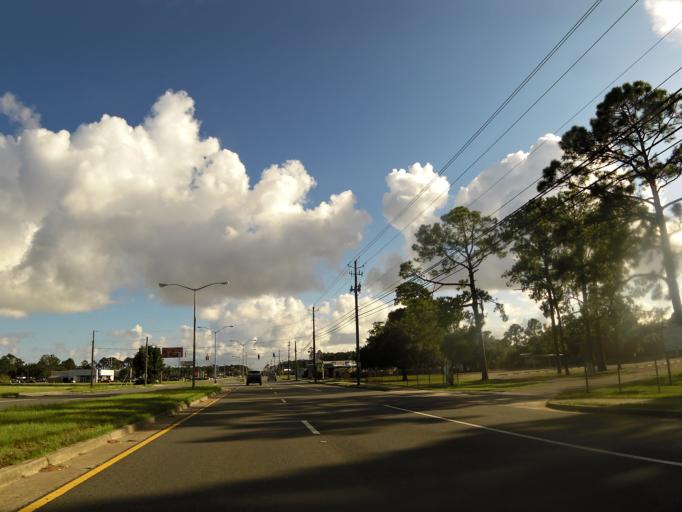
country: US
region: Georgia
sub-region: Glynn County
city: Country Club Estates
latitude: 31.2108
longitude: -81.4816
